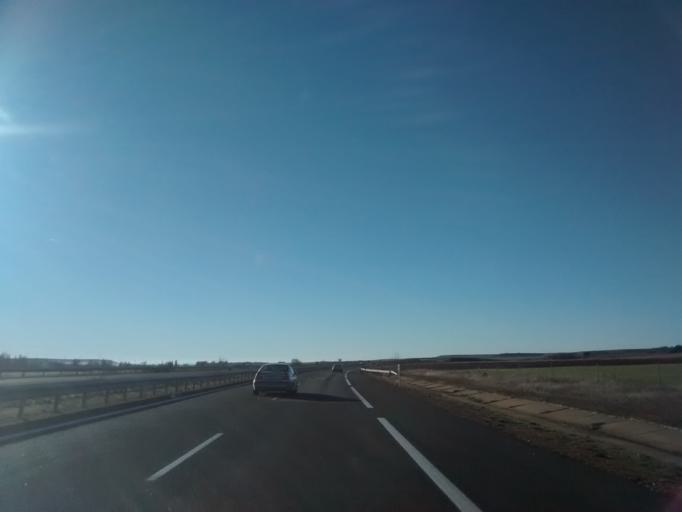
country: ES
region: Castille and Leon
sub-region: Provincia de Palencia
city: Villaprovedo
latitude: 42.5024
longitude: -4.3801
